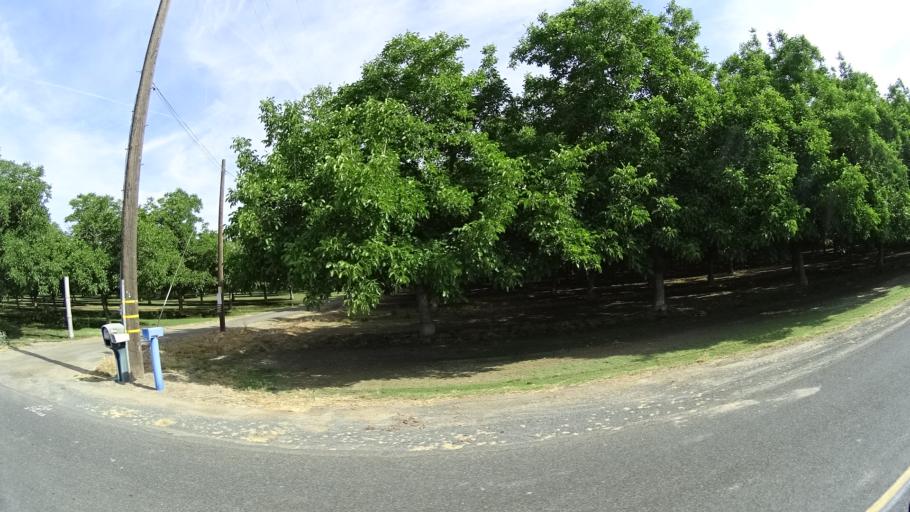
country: US
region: California
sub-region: Kings County
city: Lucerne
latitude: 36.4158
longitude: -119.6547
